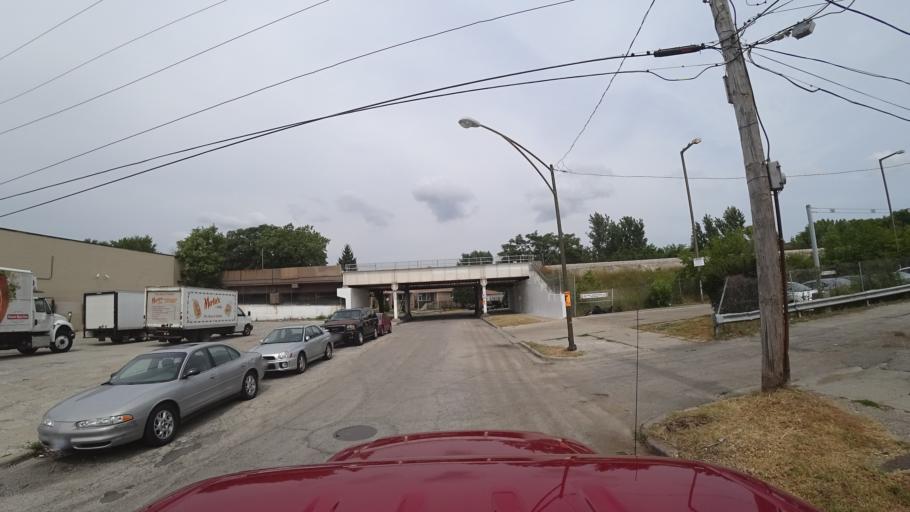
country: US
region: Illinois
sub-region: Cook County
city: Chicago
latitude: 41.8281
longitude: -87.6821
